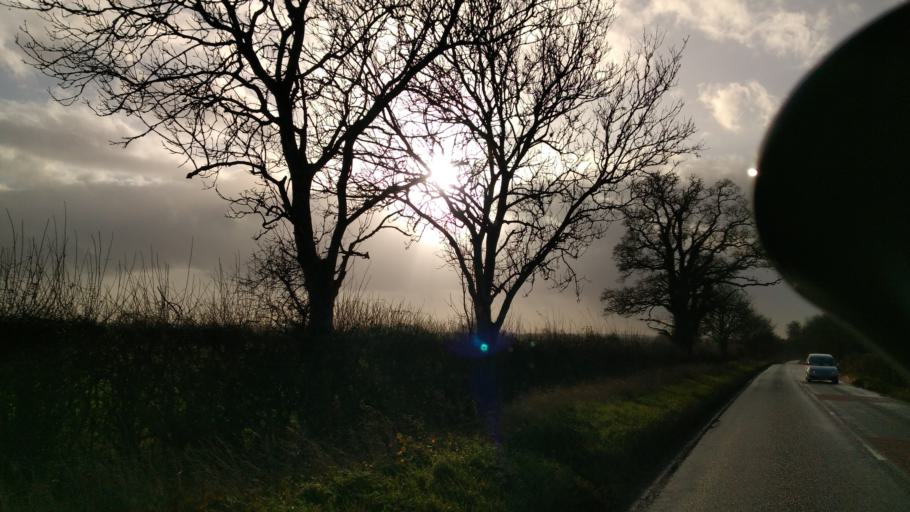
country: GB
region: England
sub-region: Wiltshire
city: Wingfield
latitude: 51.3071
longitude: -2.2572
